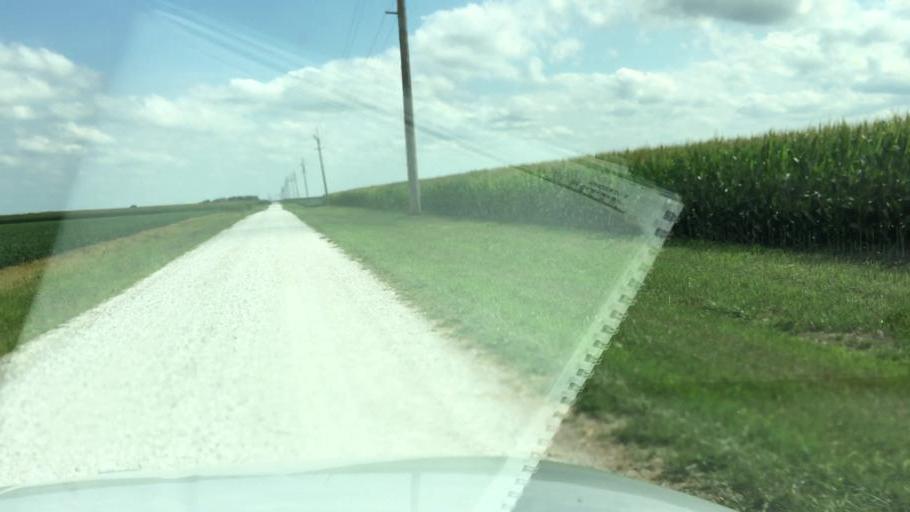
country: US
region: Illinois
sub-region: Hancock County
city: Carthage
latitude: 40.4150
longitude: -91.1784
